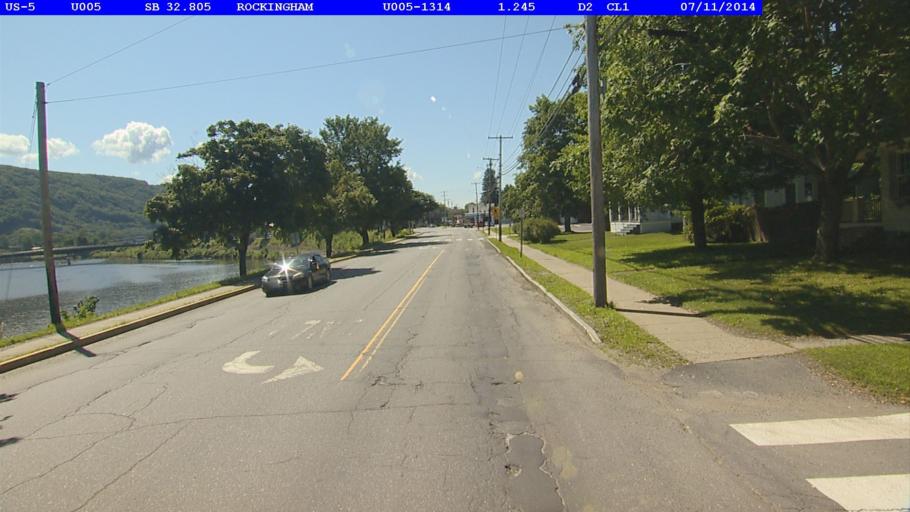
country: US
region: Vermont
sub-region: Windham County
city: Bellows Falls
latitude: 43.1401
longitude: -72.4539
